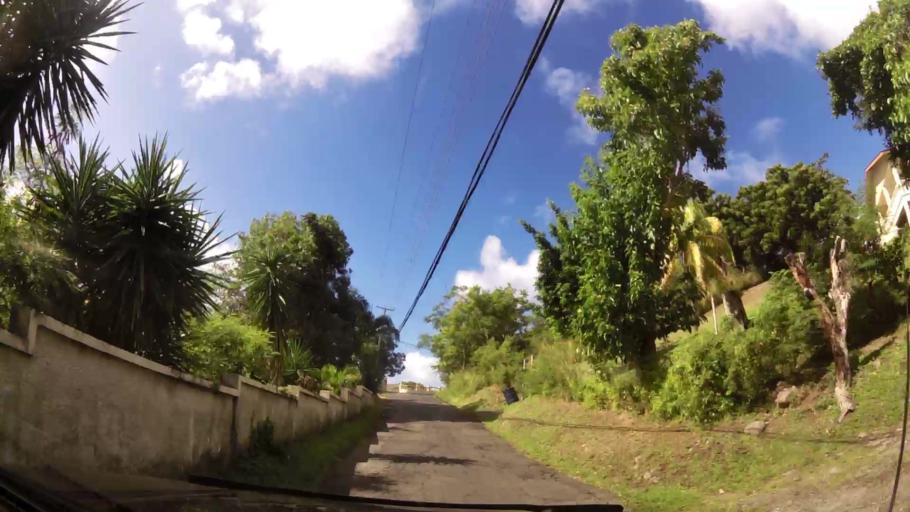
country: MS
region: Saint Peter
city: Saint Peters
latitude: 16.7533
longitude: -62.2220
